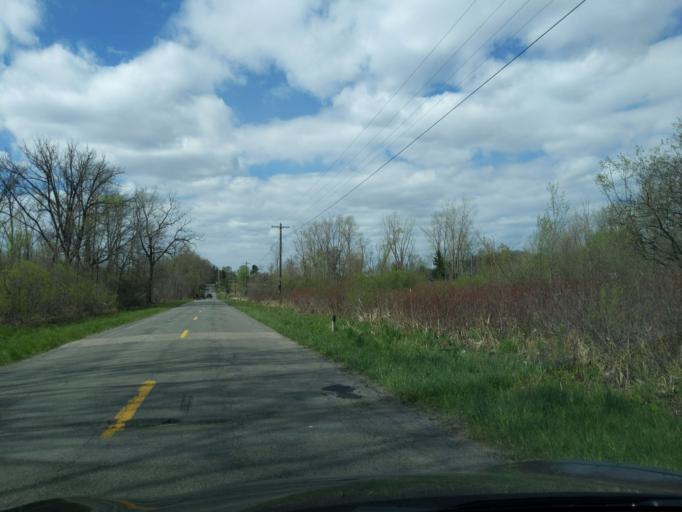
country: US
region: Michigan
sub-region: Ingham County
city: Leslie
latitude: 42.4315
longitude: -84.5409
